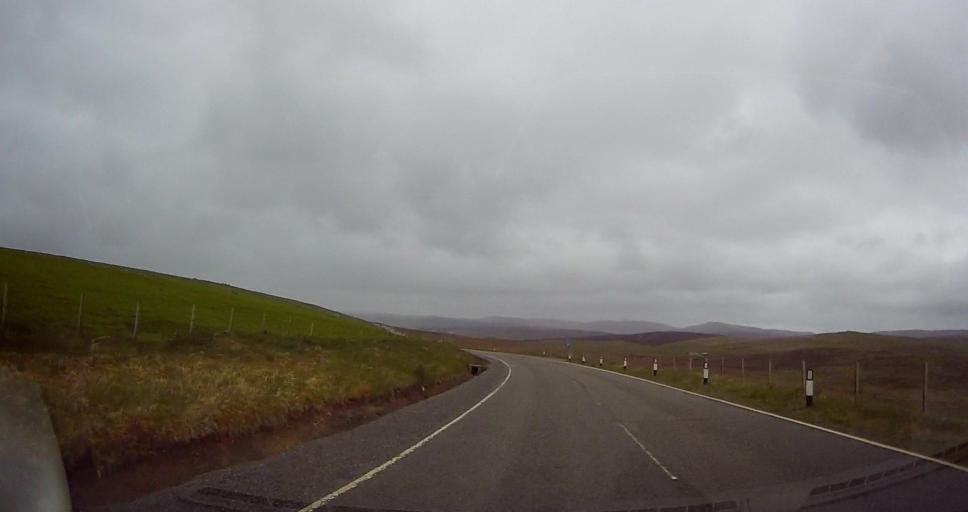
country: GB
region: Scotland
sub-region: Shetland Islands
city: Lerwick
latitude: 60.2639
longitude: -1.3993
